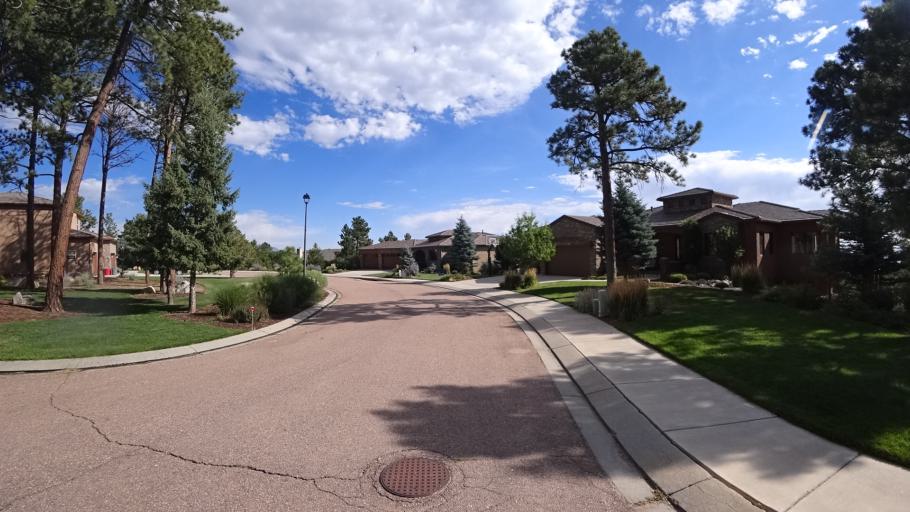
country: US
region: Colorado
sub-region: El Paso County
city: Fort Carson
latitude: 38.7615
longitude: -104.8348
